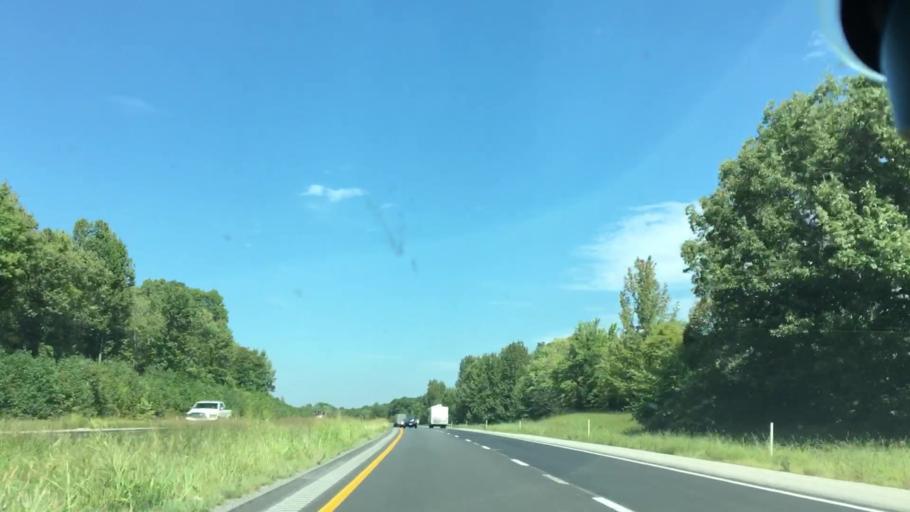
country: US
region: Kentucky
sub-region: Hopkins County
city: Madisonville
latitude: 37.3858
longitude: -87.4793
